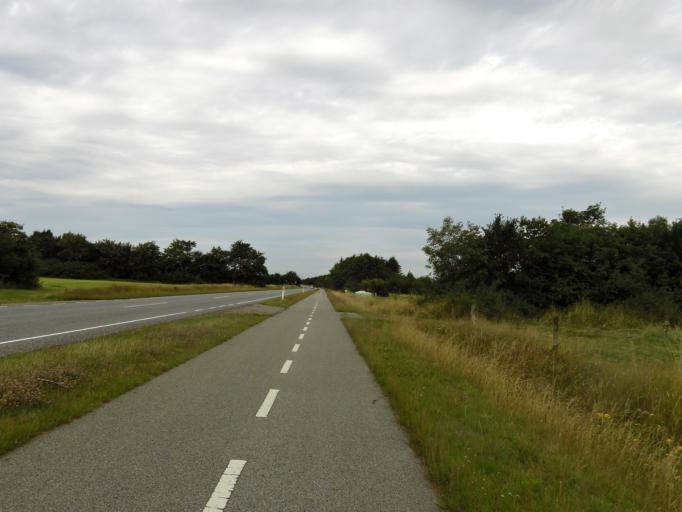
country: DK
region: South Denmark
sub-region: Esbjerg Kommune
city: Ribe
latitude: 55.3119
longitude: 8.8240
